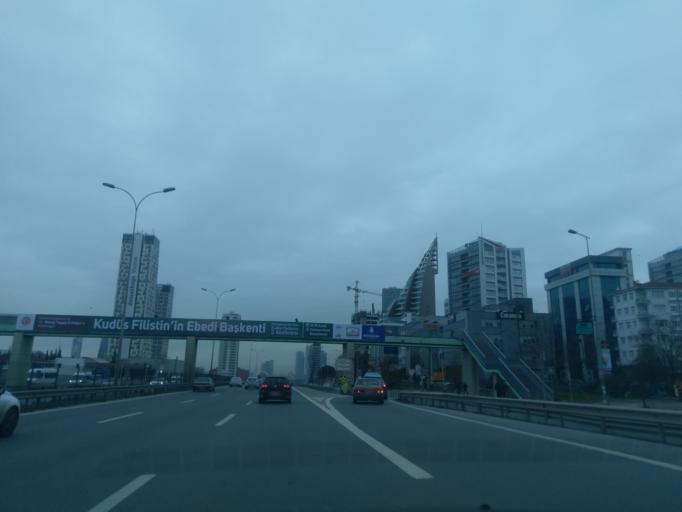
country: TR
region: Istanbul
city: Maltepe
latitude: 40.9087
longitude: 29.2049
